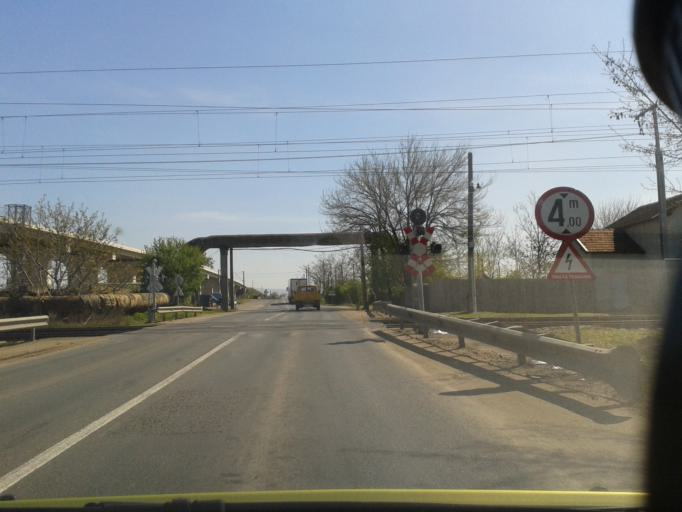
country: RO
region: Arad
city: Arad
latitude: 46.2158
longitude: 21.3228
